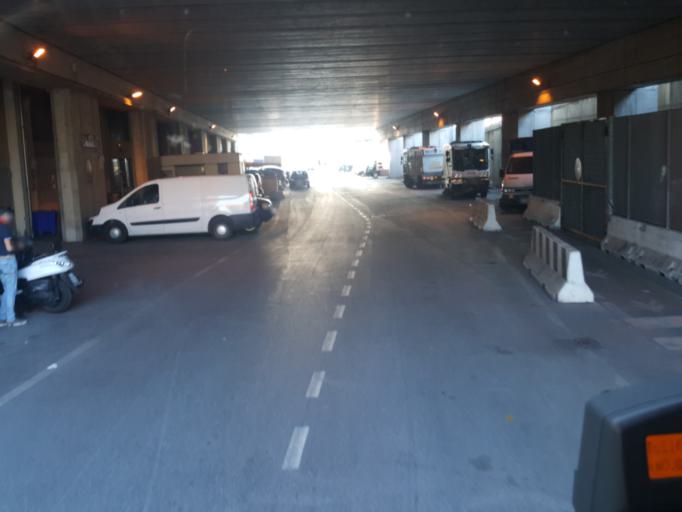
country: IT
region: Liguria
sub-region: Provincia di Genova
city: San Teodoro
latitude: 44.4069
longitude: 8.9080
